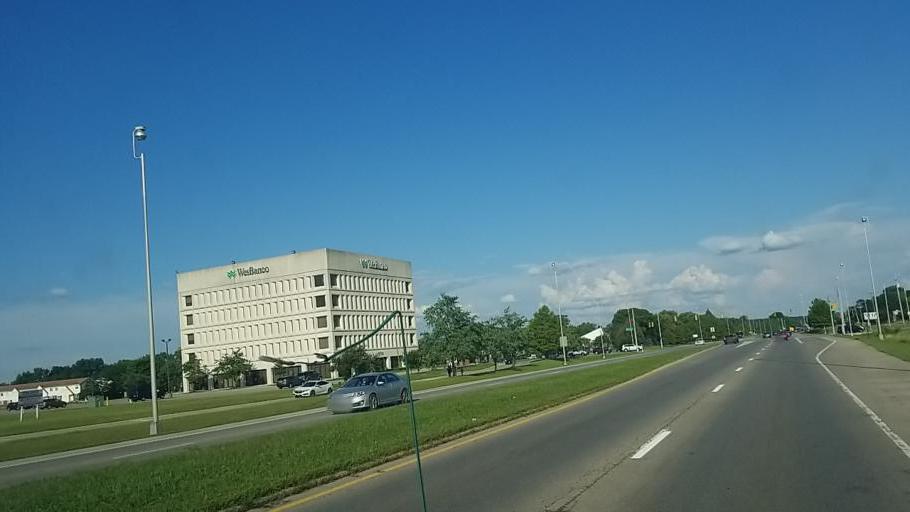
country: US
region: Ohio
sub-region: Franklin County
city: Minerva Park
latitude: 40.0842
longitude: -82.9473
